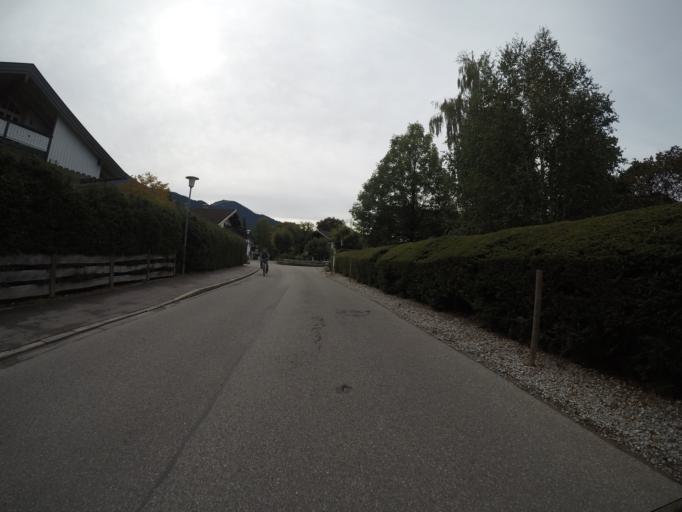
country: DE
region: Bavaria
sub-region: Upper Bavaria
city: Rottach-Egern
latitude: 47.6937
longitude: 11.7599
